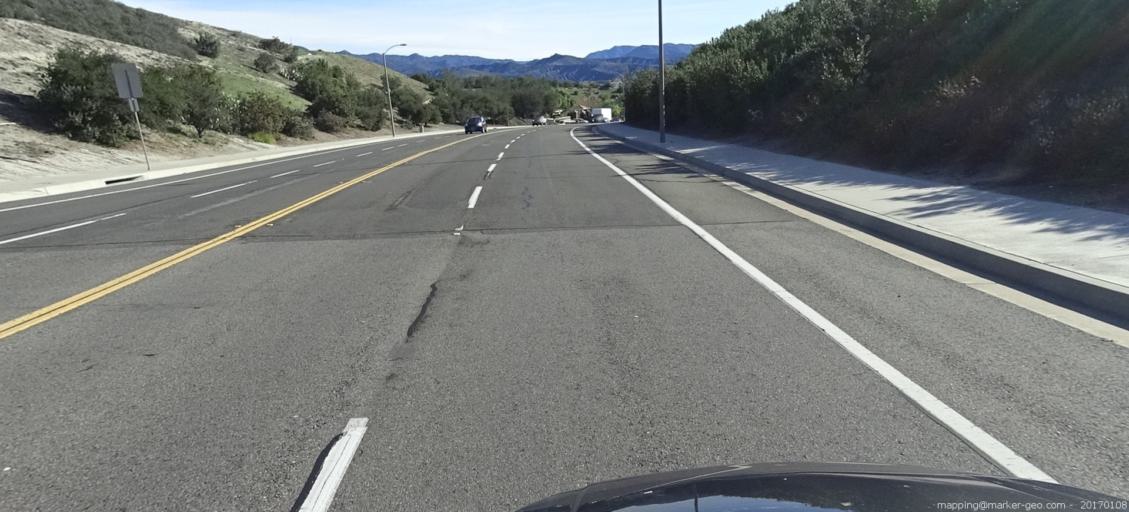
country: US
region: California
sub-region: Orange County
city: Coto De Caza
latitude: 33.5896
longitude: -117.6016
